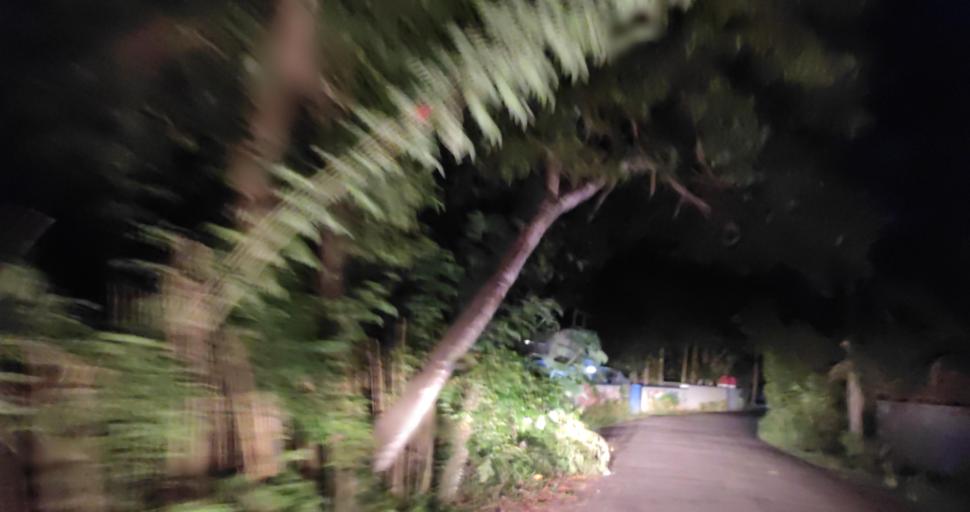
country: IN
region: Kerala
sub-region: Alappuzha
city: Shertallai
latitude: 9.6296
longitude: 76.3434
